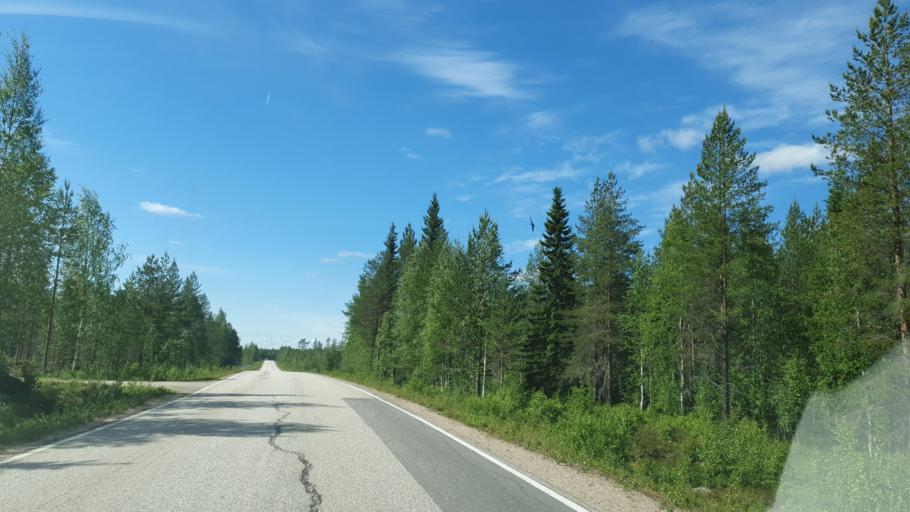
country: FI
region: Kainuu
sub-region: Kehys-Kainuu
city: Suomussalmi
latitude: 64.5704
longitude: 28.9921
